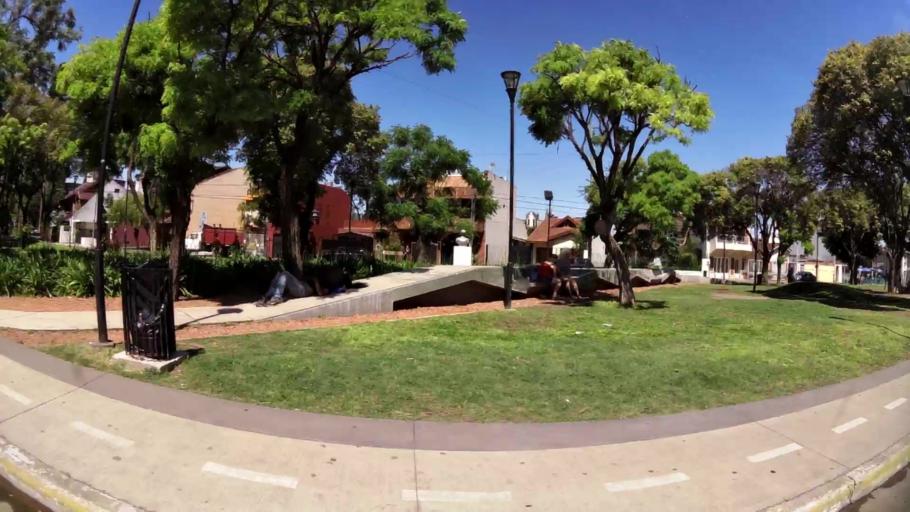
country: AR
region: Buenos Aires
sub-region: Partido de General San Martin
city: General San Martin
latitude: -34.5644
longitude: -58.5508
